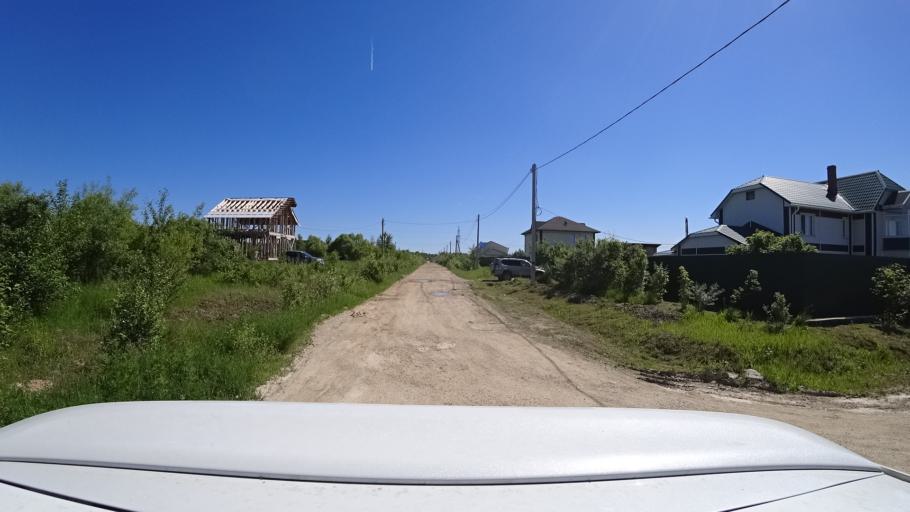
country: RU
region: Khabarovsk Krai
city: Topolevo
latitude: 48.5653
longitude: 135.1926
